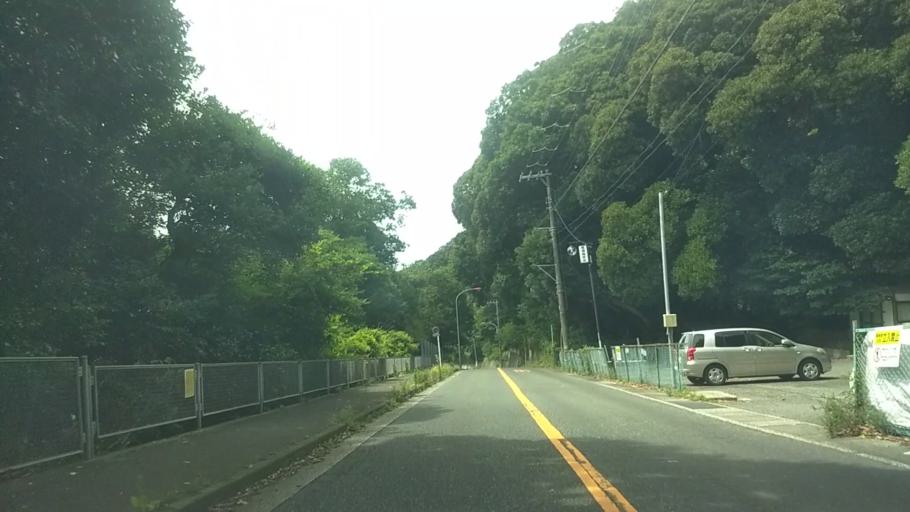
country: JP
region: Kanagawa
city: Yokosuka
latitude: 35.2591
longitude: 139.7177
